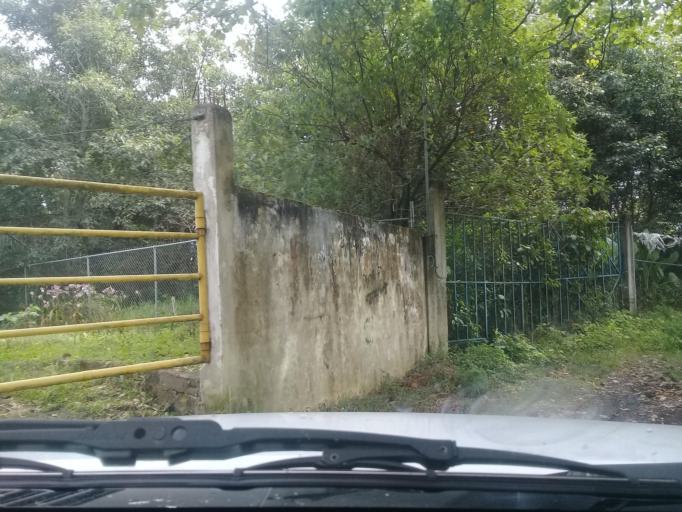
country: MX
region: Veracruz
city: Rafael Lucio
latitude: 19.5913
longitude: -96.9940
